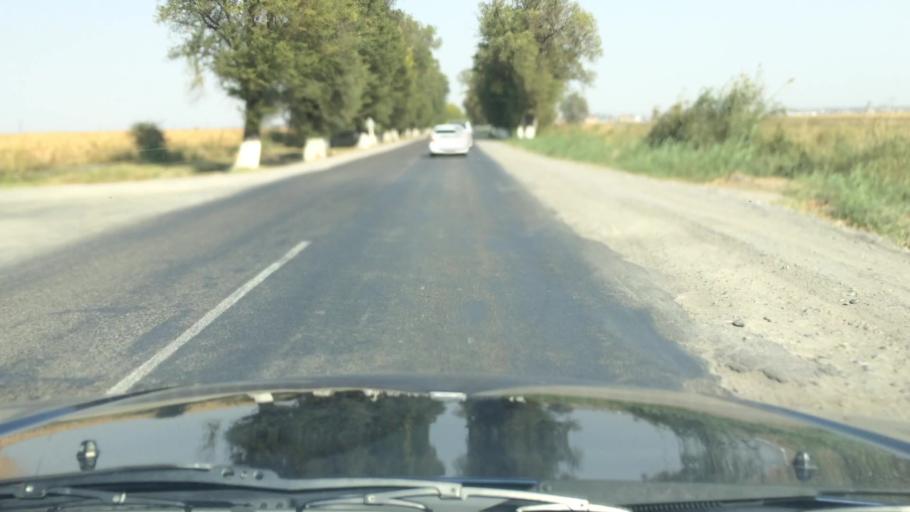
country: KG
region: Chuy
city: Lebedinovka
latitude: 42.9013
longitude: 74.6854
